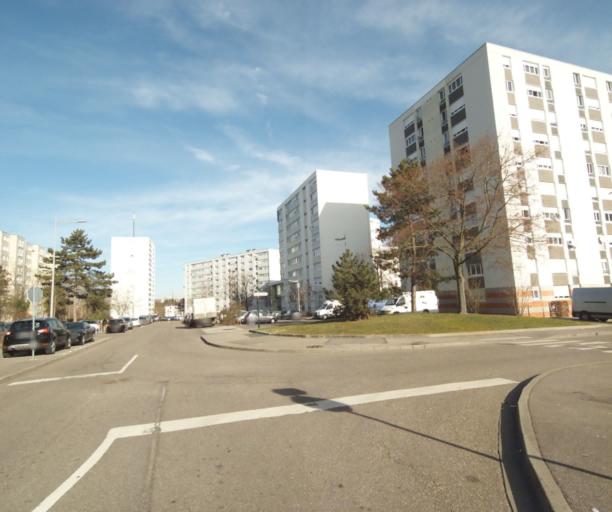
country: FR
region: Lorraine
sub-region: Departement de Meurthe-et-Moselle
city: Vandoeuvre-les-Nancy
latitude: 48.6603
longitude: 6.1828
